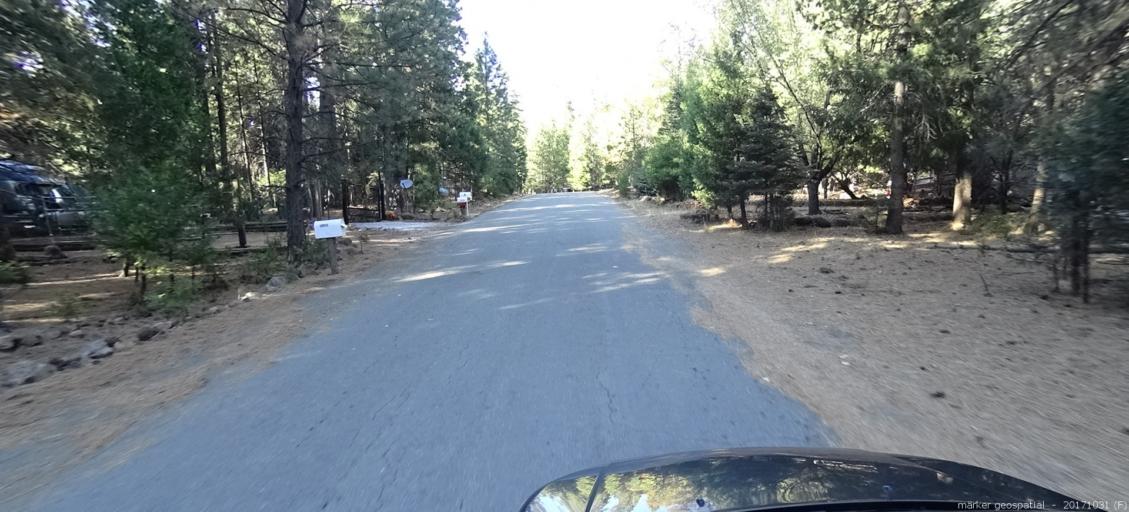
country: US
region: California
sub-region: Shasta County
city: Shingletown
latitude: 40.5022
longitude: -121.9057
